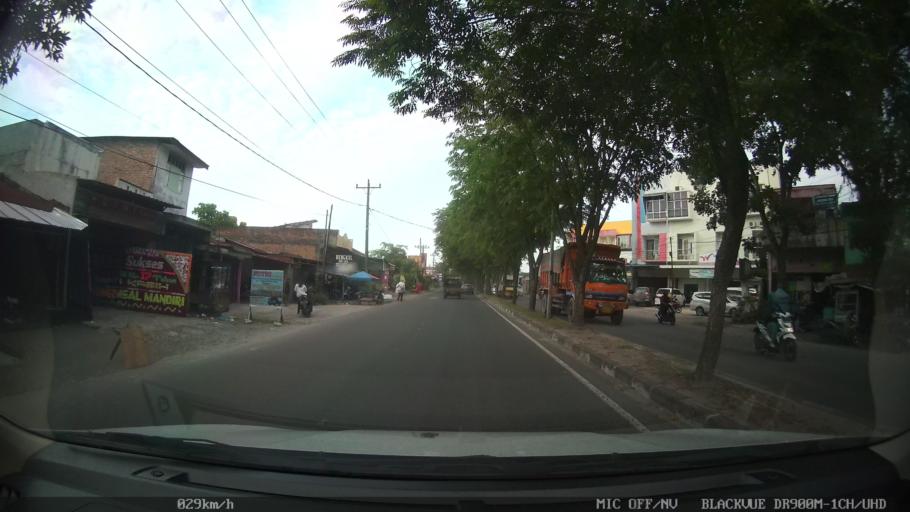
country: ID
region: North Sumatra
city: Sunggal
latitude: 3.5522
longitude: 98.6111
